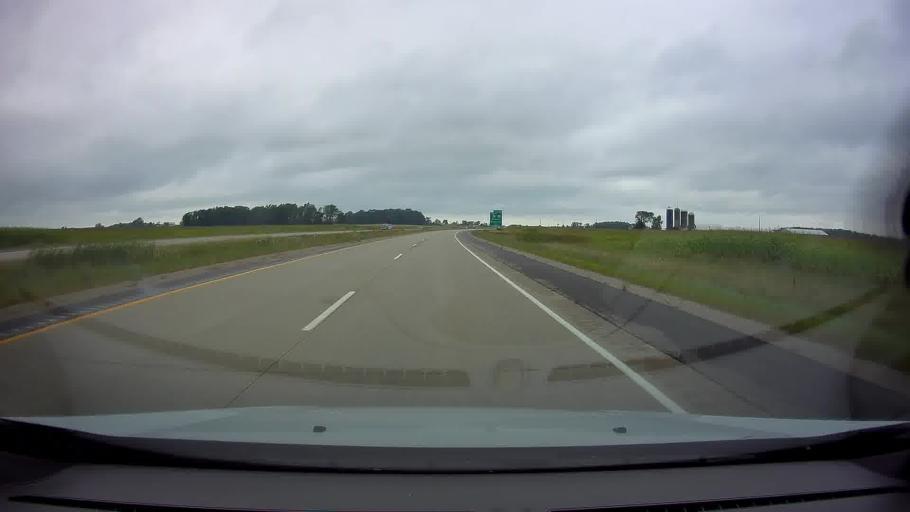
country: US
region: Wisconsin
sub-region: Brown County
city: Pulaski
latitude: 44.6550
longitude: -88.3003
